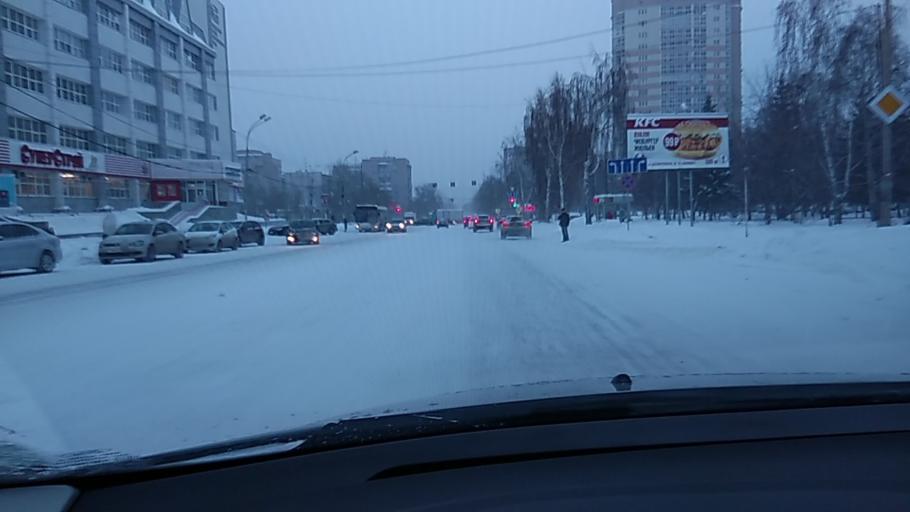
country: RU
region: Sverdlovsk
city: Sovkhoznyy
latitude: 56.8199
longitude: 60.5555
